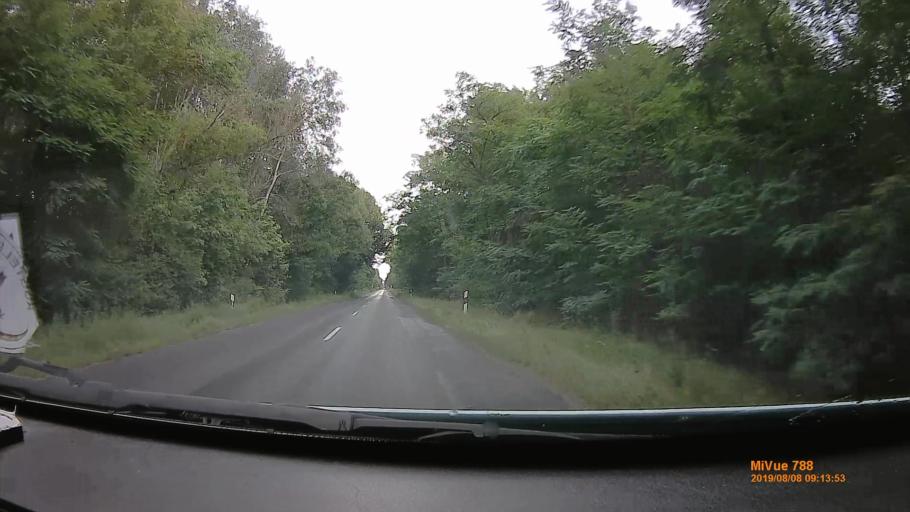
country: HU
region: Hajdu-Bihar
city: Hajdusamson
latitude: 47.5268
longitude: 21.7406
